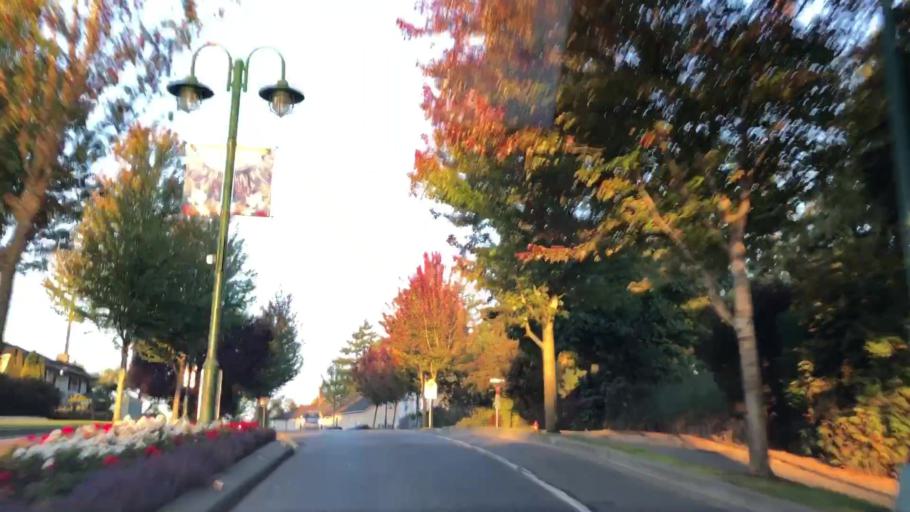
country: CA
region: British Columbia
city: Colwood
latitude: 48.4571
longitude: -123.4390
